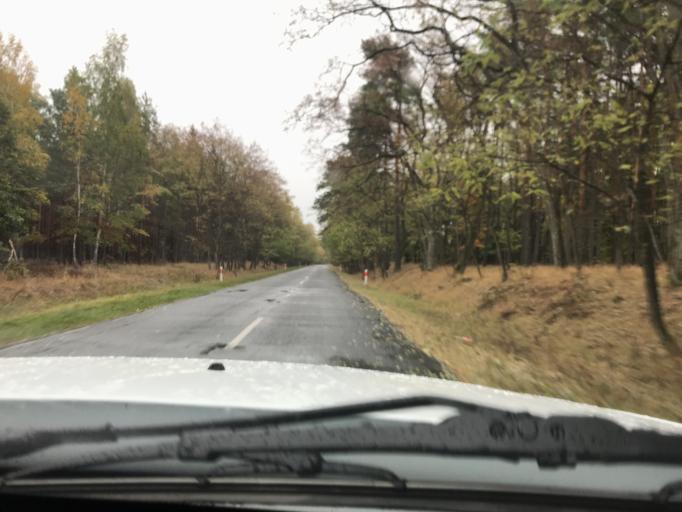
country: PL
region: West Pomeranian Voivodeship
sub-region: Powiat gryfinski
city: Moryn
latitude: 52.7766
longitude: 14.3663
